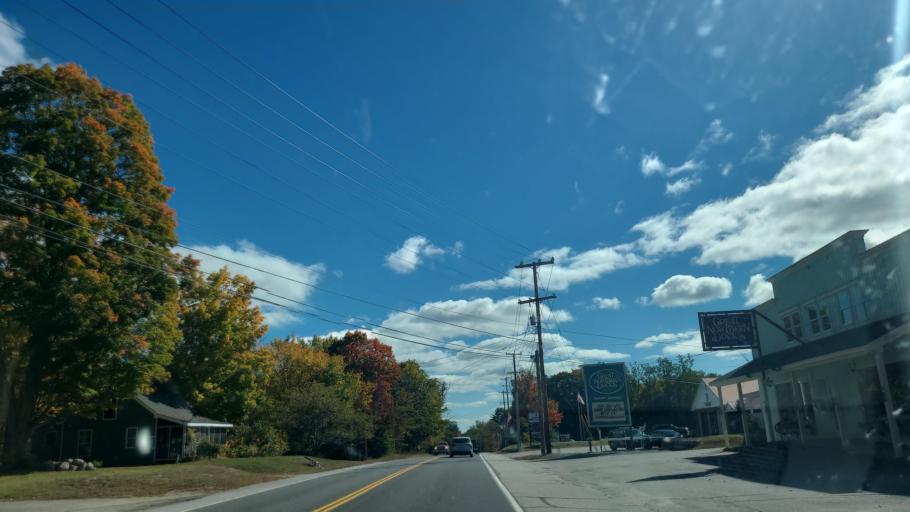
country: US
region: Maine
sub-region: Cumberland County
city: Bridgton
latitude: 43.9735
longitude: -70.6141
